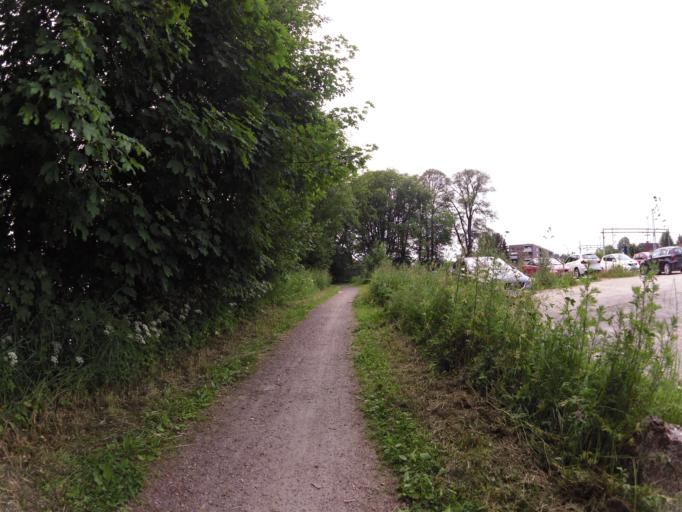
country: NO
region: Ostfold
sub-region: Fredrikstad
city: Fredrikstad
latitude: 59.2091
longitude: 10.9560
